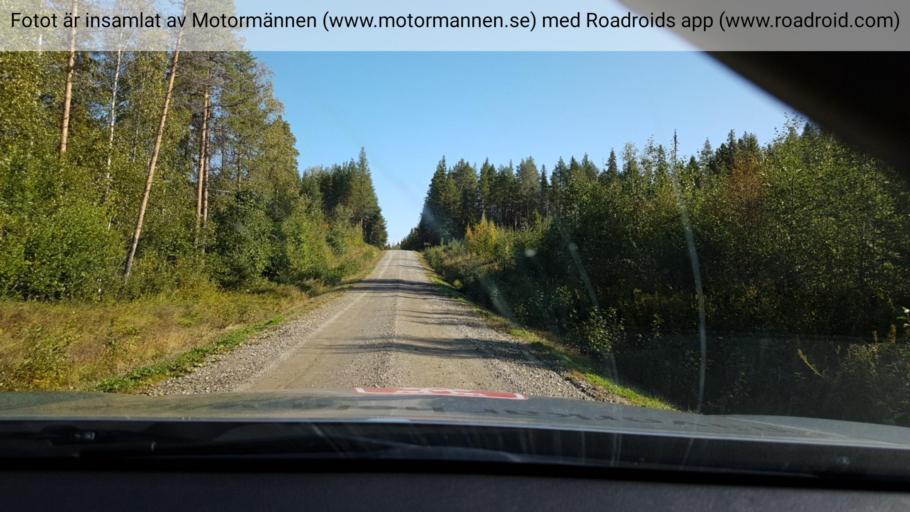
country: SE
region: Vaesterbotten
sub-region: Norsjo Kommun
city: Norsjoe
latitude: 64.6742
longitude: 19.3813
